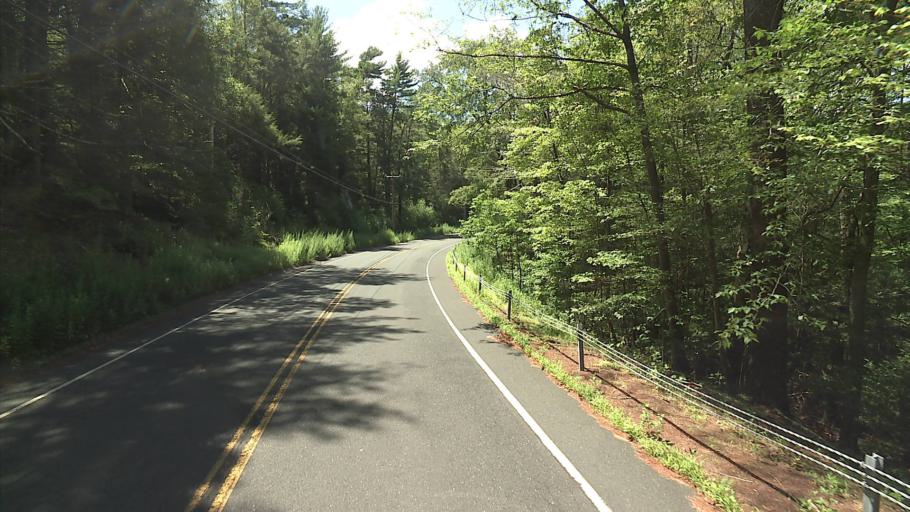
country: US
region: Connecticut
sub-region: Litchfield County
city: New Hartford Center
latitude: 41.9062
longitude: -72.9524
